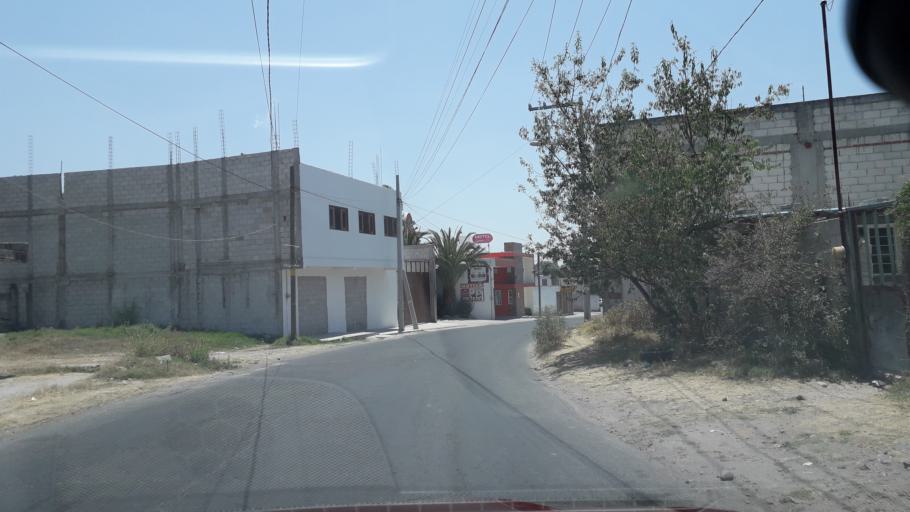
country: MX
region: Puebla
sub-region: Puebla
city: Articulo Primero Constitucional
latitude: 18.9898
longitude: -98.1837
